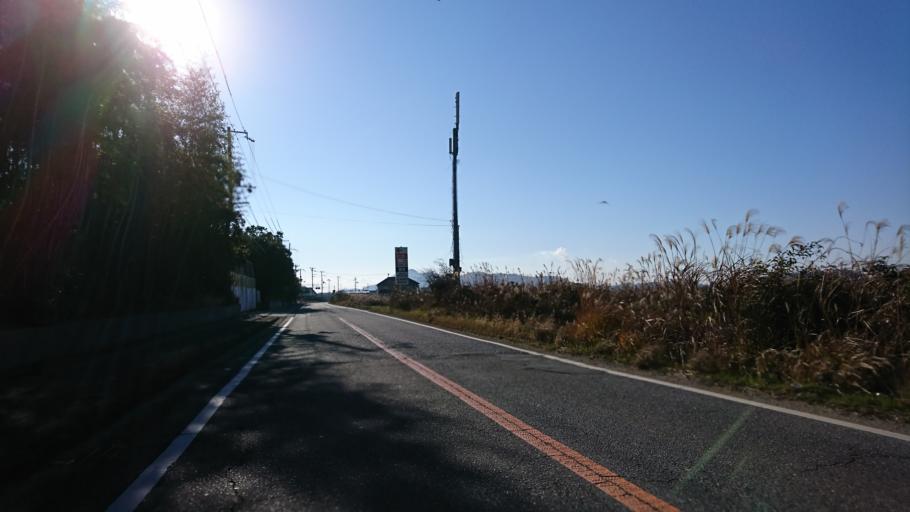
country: JP
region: Hyogo
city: Kakogawacho-honmachi
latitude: 34.8415
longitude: 134.8377
